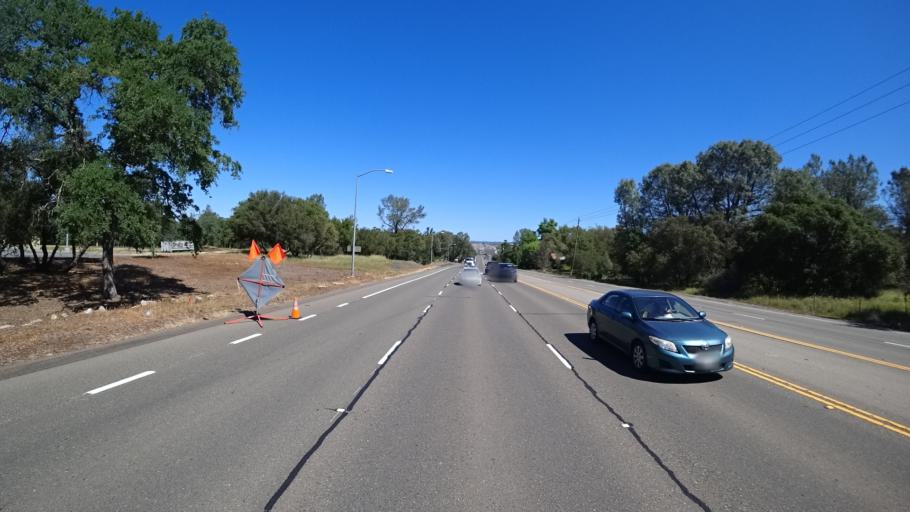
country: US
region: California
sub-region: Placer County
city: Rocklin
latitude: 38.7938
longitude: -121.2059
